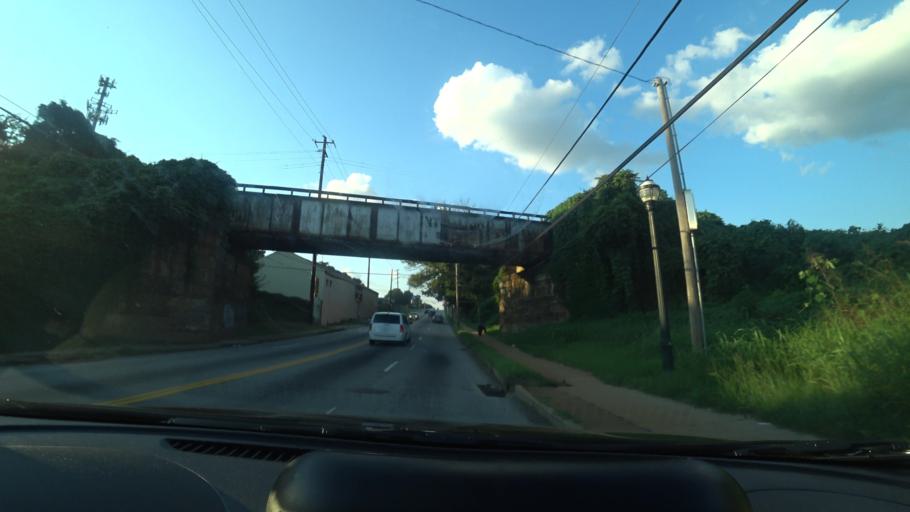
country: US
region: Georgia
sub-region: Fulton County
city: Atlanta
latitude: 33.7193
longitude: -84.3933
